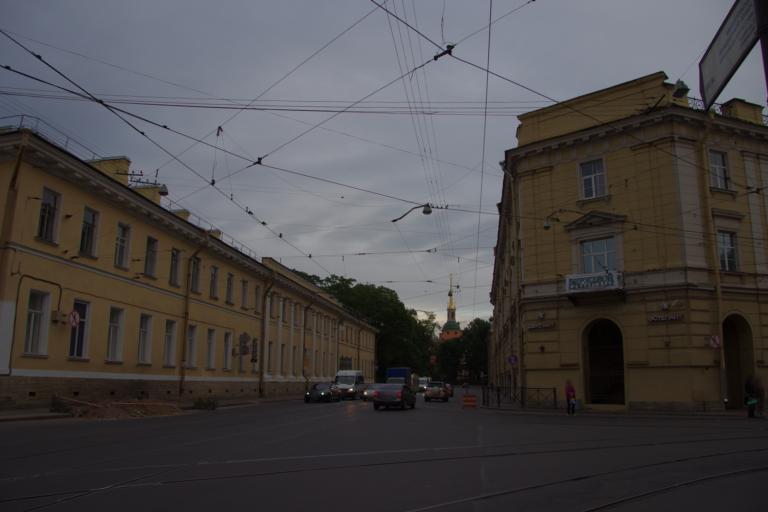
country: RU
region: St.-Petersburg
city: Saint Petersburg
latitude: 59.9373
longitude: 30.3364
